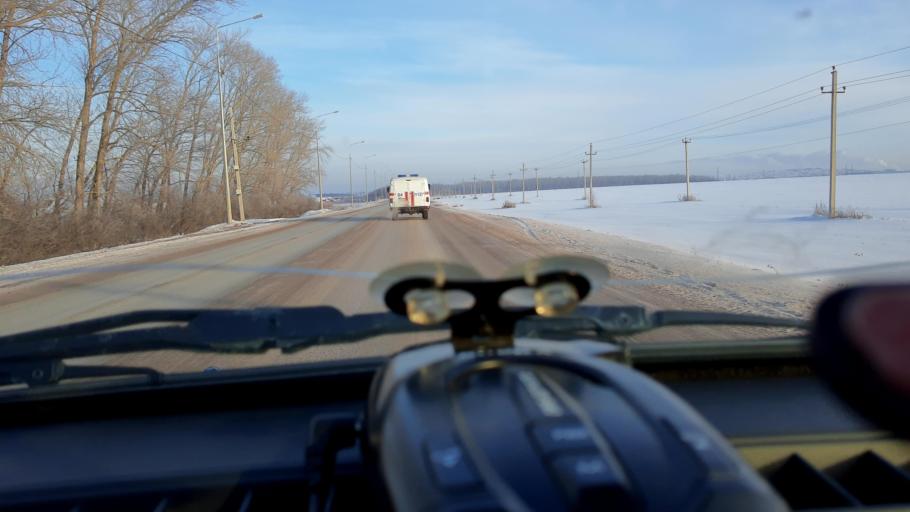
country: RU
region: Bashkortostan
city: Avdon
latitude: 54.6062
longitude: 55.8550
